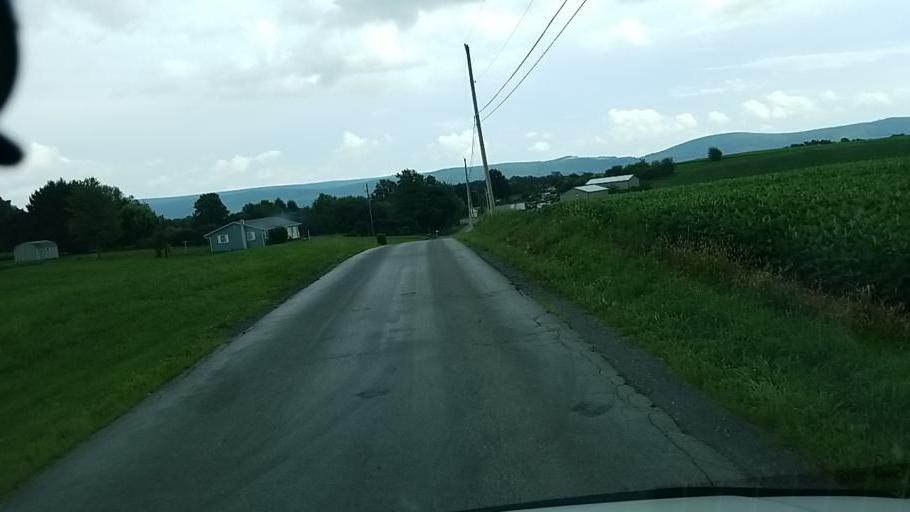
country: US
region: Pennsylvania
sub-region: Dauphin County
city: Elizabethville
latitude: 40.5944
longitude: -76.8286
